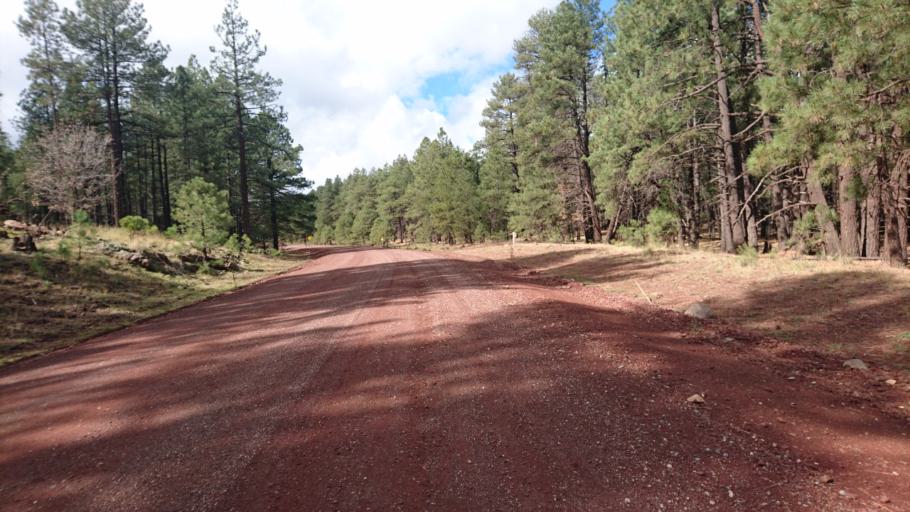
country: US
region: Arizona
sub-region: Coconino County
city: Parks
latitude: 35.2753
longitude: -111.8994
